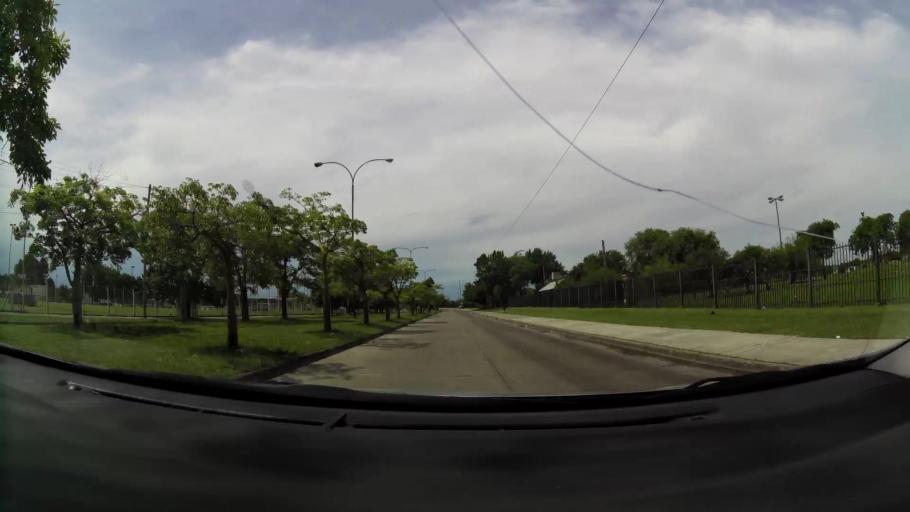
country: AR
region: Buenos Aires F.D.
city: Villa Lugano
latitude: -34.6622
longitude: -58.4665
